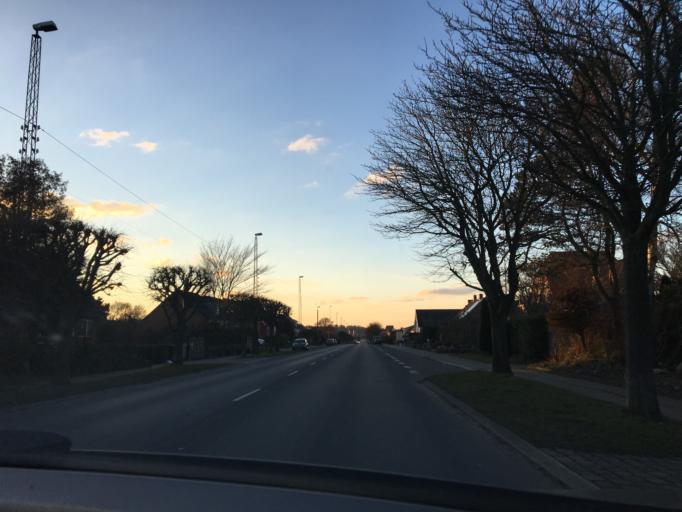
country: DK
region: South Denmark
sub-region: Middelfart Kommune
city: Middelfart
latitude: 55.4994
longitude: 9.7579
